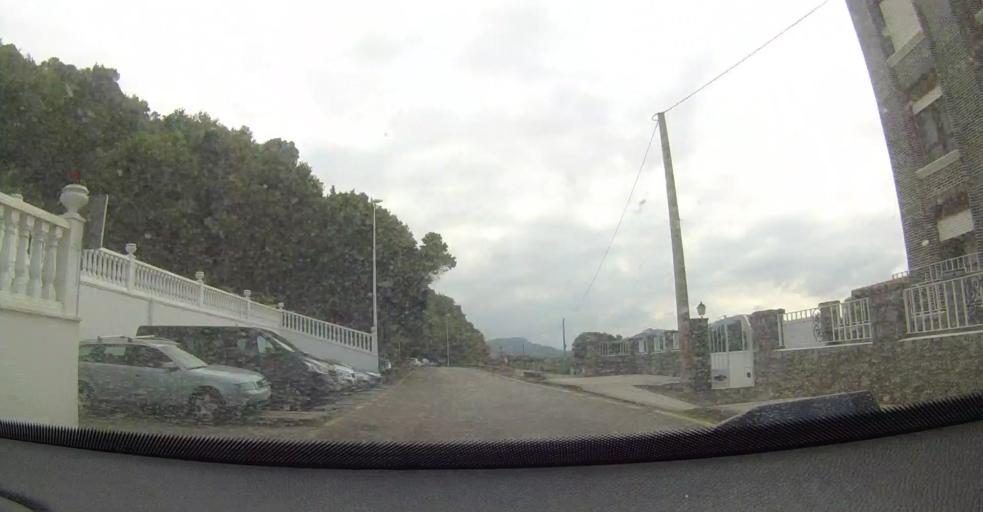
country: ES
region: Cantabria
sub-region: Provincia de Cantabria
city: Noja
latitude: 43.4703
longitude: -3.5108
